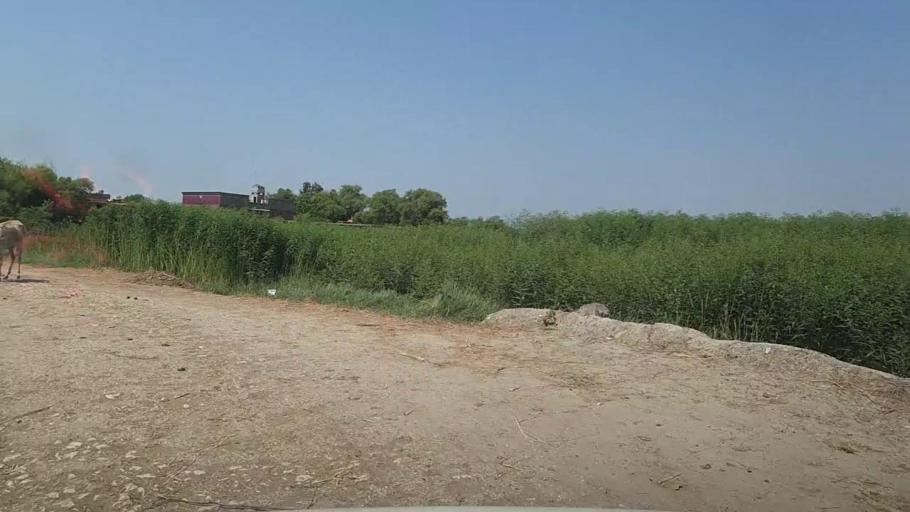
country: PK
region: Sindh
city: Ubauro
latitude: 28.1980
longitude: 69.8023
